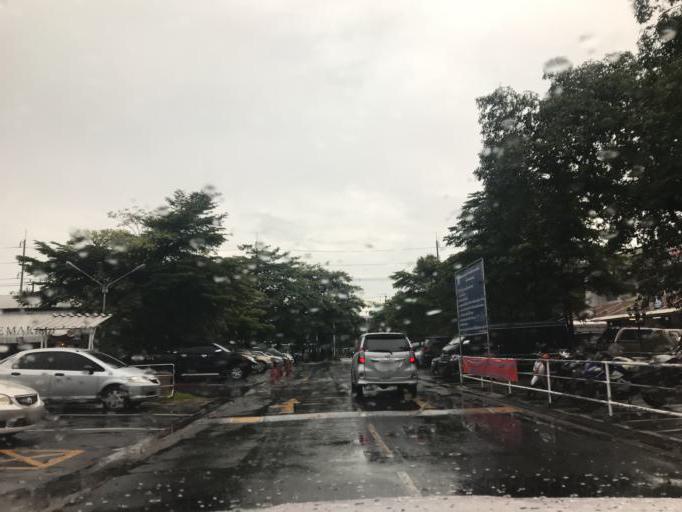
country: TH
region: Bangkok
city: Bangkok Noi
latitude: 13.7515
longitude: 100.4790
